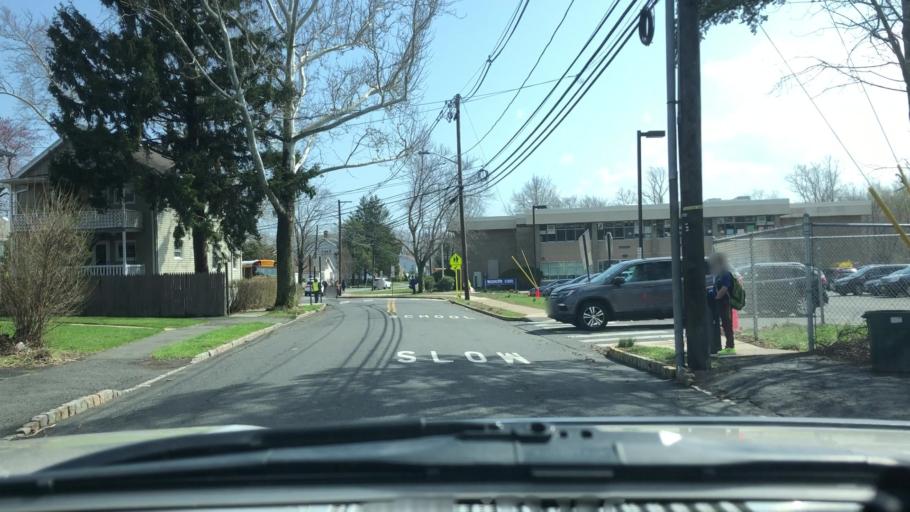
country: US
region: New Jersey
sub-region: Union County
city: Springfield
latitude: 40.7204
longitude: -74.3100
